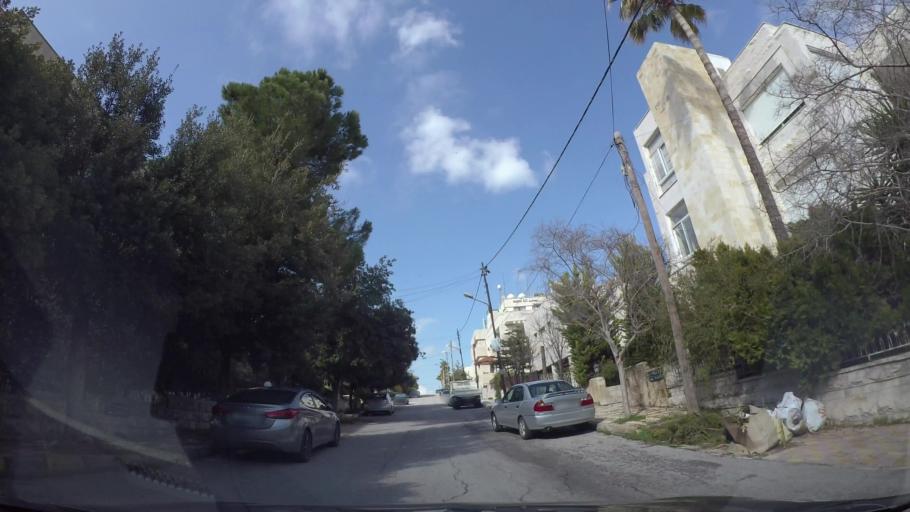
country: JO
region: Amman
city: Amman
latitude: 31.9724
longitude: 35.8900
